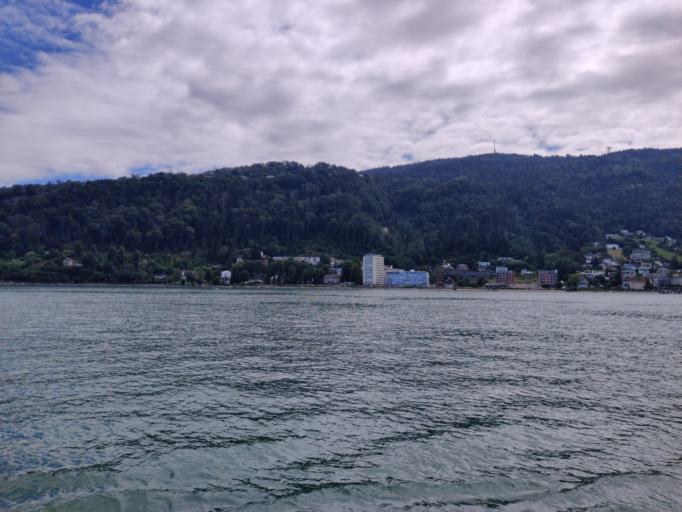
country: AT
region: Vorarlberg
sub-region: Politischer Bezirk Bregenz
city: Bregenz
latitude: 47.5123
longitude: 9.7452
